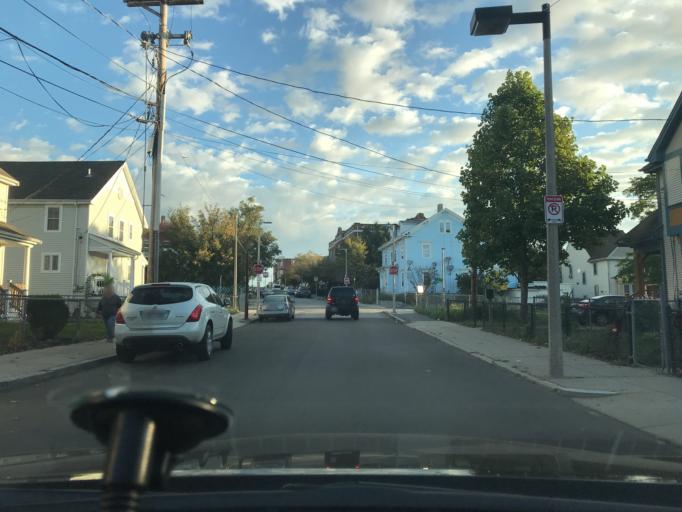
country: US
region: Massachusetts
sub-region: Suffolk County
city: South Boston
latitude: 42.3128
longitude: -71.0726
